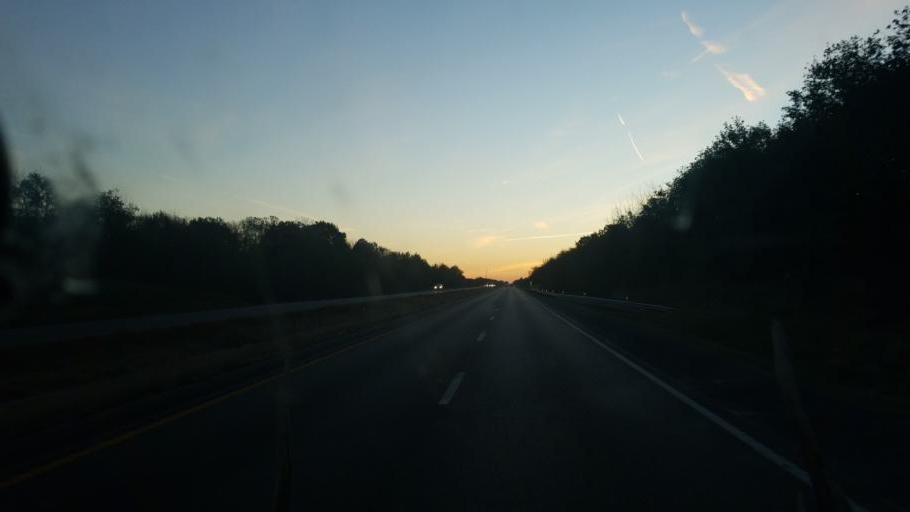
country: US
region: Missouri
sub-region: Cooper County
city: Boonville
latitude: 38.9384
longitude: -92.6490
